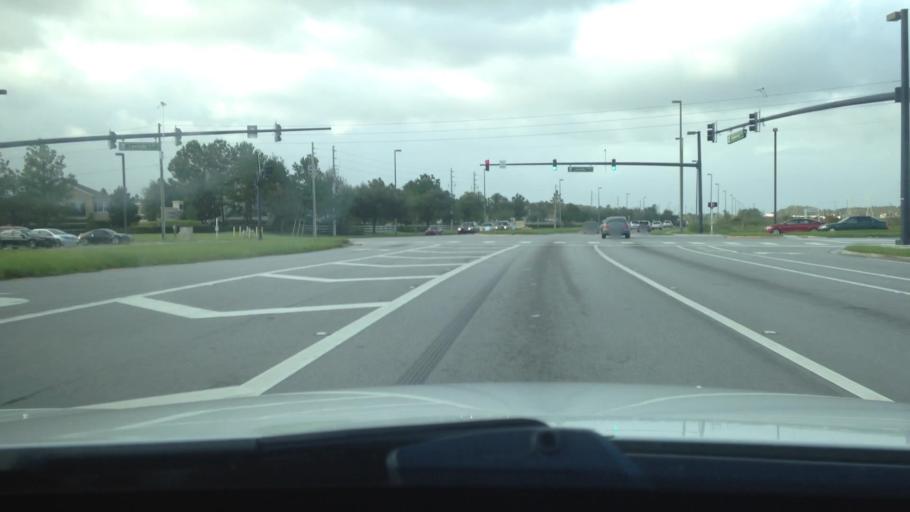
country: US
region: Florida
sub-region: Orange County
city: Conway
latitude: 28.4656
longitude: -81.2897
